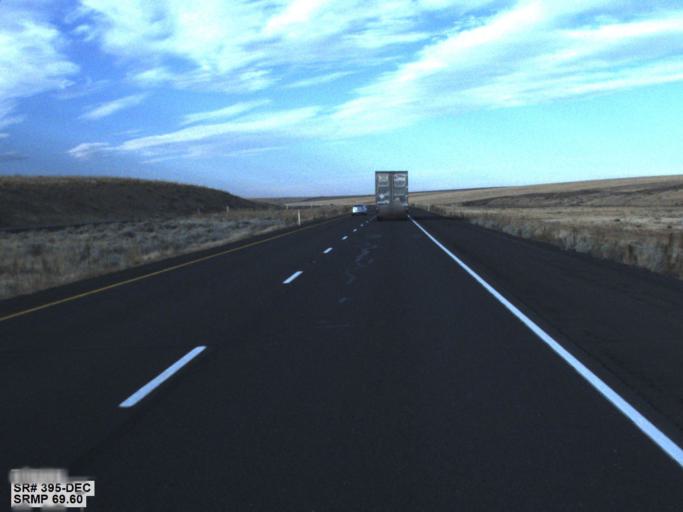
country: US
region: Washington
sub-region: Franklin County
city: Connell
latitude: 46.8184
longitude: -118.6941
